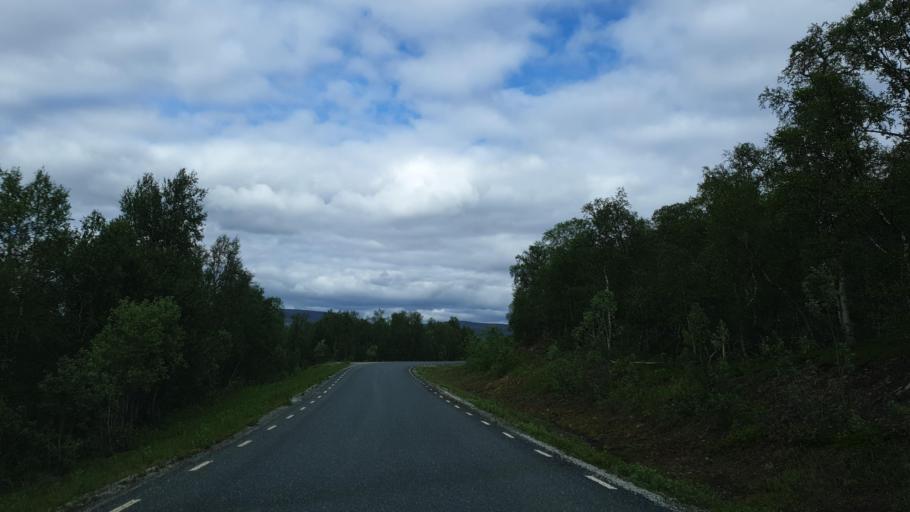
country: NO
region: Nordland
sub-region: Hattfjelldal
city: Hattfjelldal
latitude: 65.4208
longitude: 14.8772
